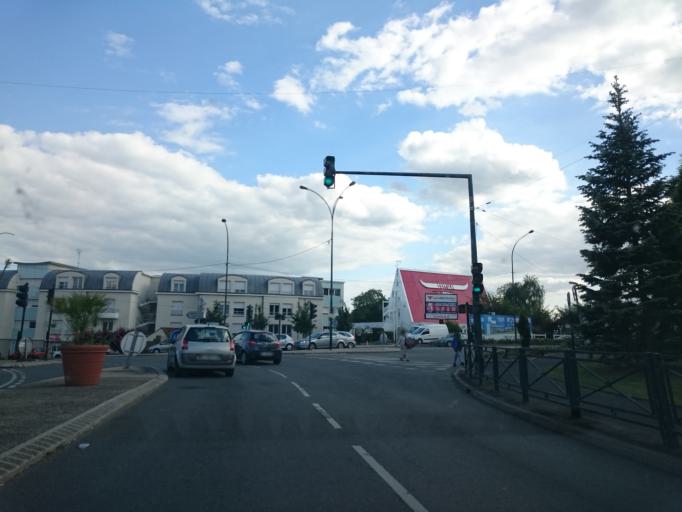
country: FR
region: Ile-de-France
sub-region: Departement de l'Essonne
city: Villabe
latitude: 48.6115
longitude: 2.4613
